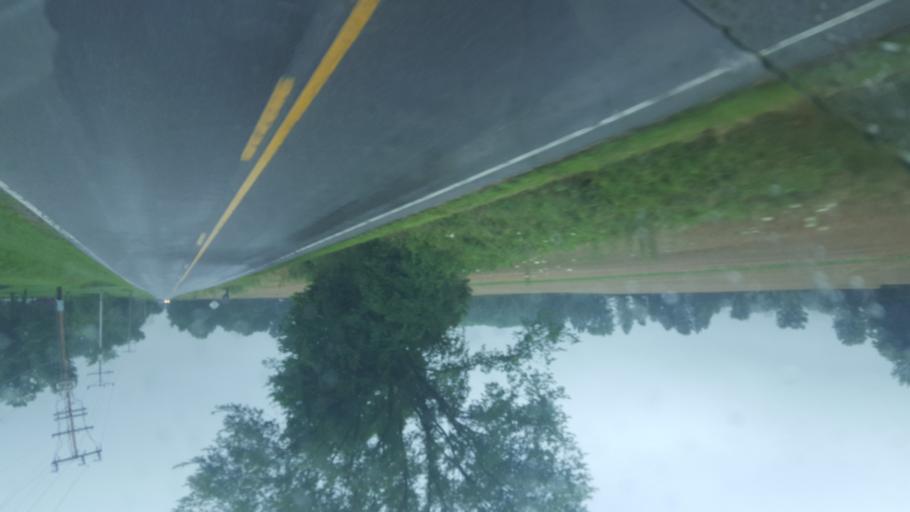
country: US
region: Ohio
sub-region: Delaware County
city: Sunbury
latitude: 40.2463
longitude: -82.9117
